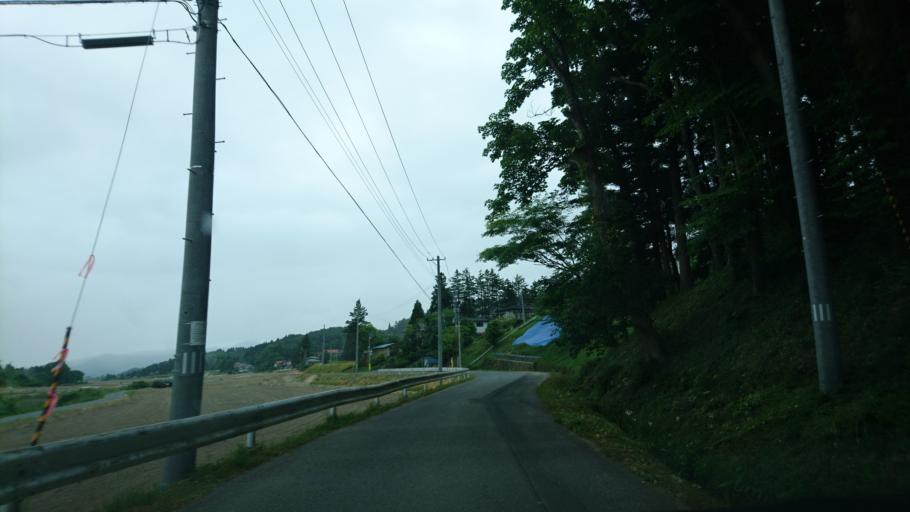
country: JP
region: Iwate
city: Ichinoseki
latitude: 38.9062
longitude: 141.1792
